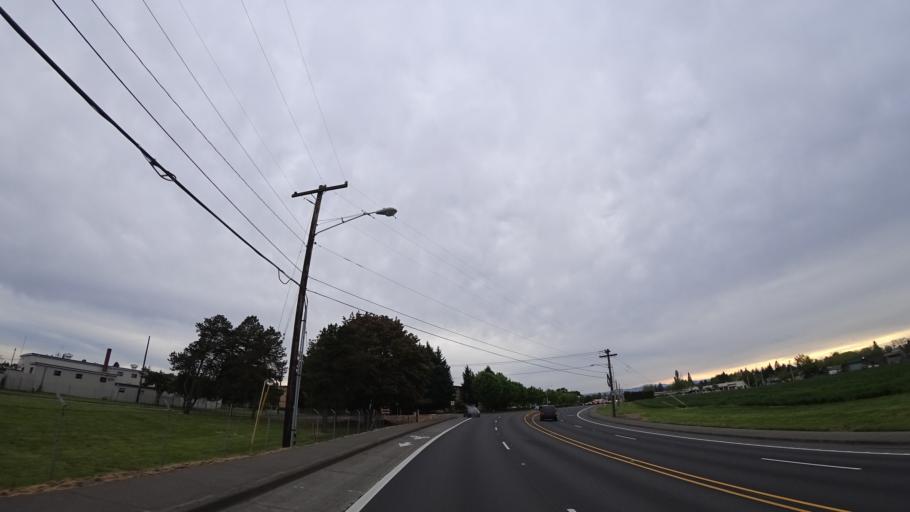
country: US
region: Oregon
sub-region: Washington County
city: Hillsboro
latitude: 45.5308
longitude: -122.9532
